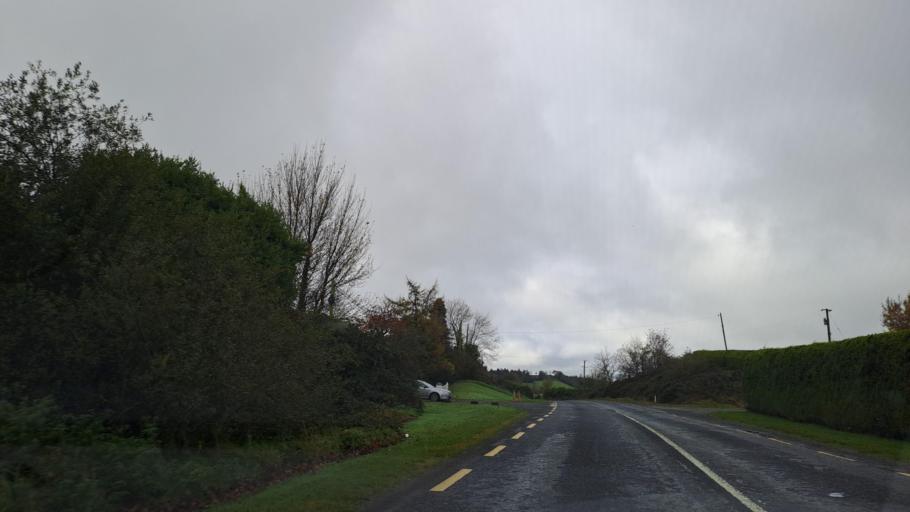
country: IE
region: Ulster
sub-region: An Cabhan
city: Bailieborough
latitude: 53.9043
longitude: -6.9965
